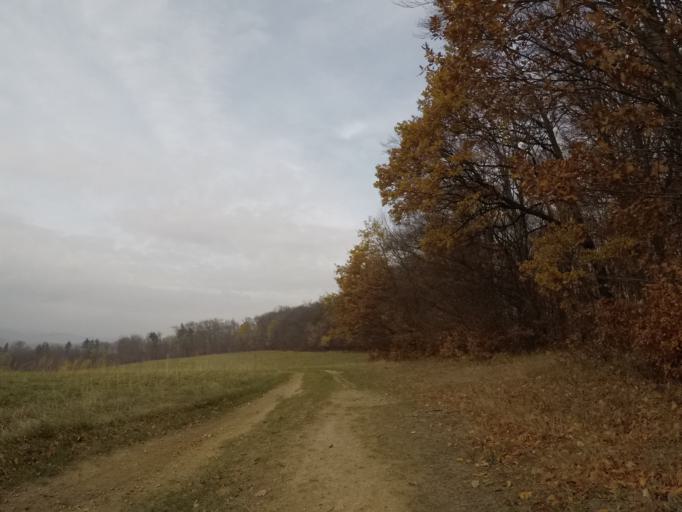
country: SK
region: Presovsky
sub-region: Okres Presov
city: Presov
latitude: 48.9341
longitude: 21.1290
